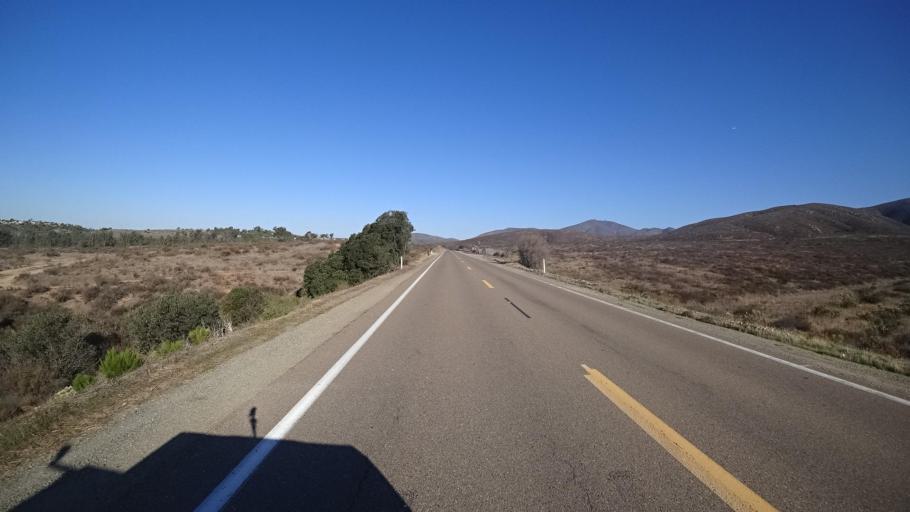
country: US
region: California
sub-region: San Diego County
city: Jamul
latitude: 32.6424
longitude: -116.9248
